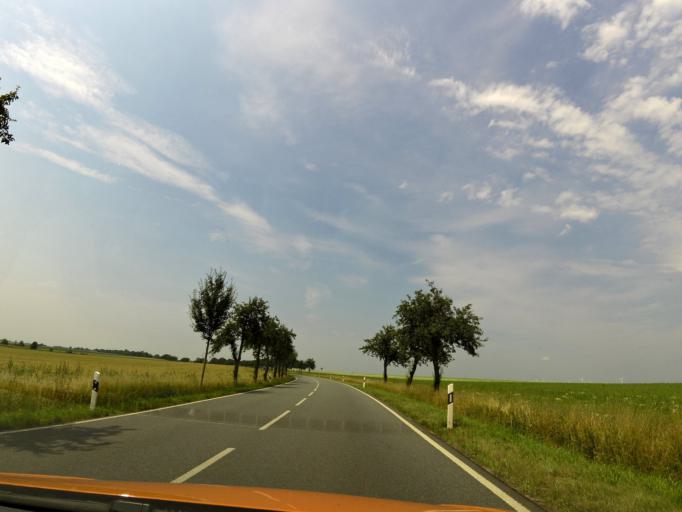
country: DE
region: Brandenburg
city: Kyritz
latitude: 52.9628
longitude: 12.3929
